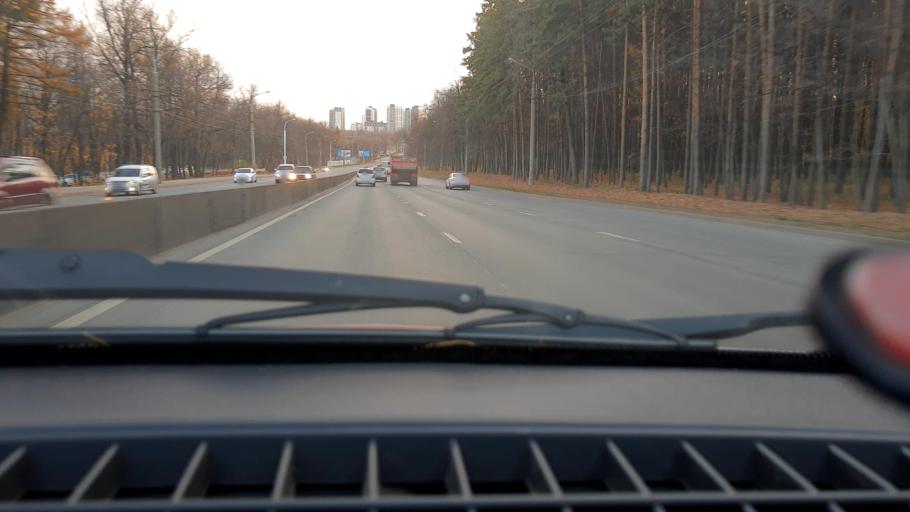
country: RU
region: Bashkortostan
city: Ufa
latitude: 54.7362
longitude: 56.0269
